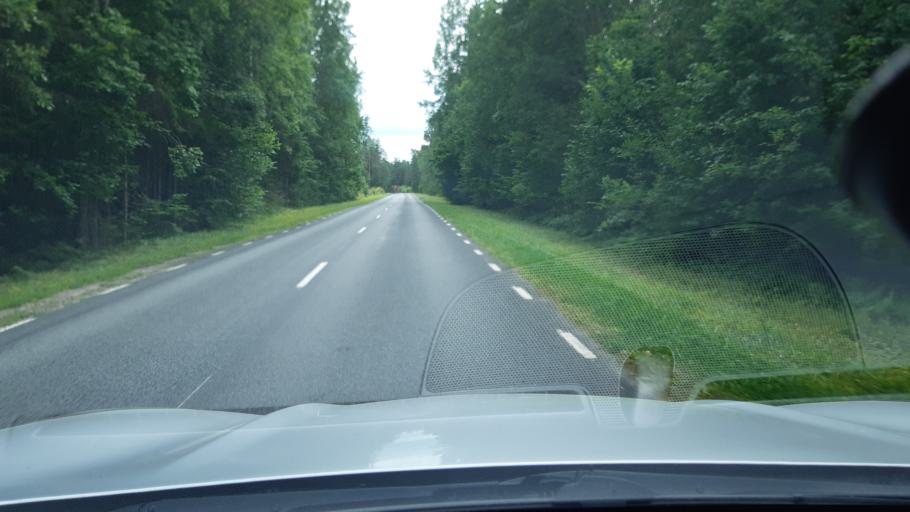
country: EE
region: Raplamaa
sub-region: Maerjamaa vald
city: Marjamaa
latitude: 59.0312
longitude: 24.5532
